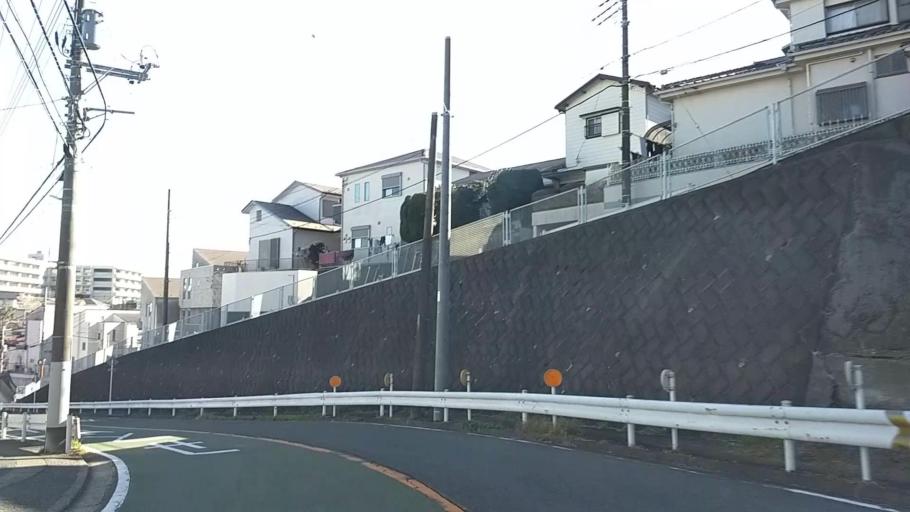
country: JP
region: Kanagawa
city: Yokohama
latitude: 35.4505
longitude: 139.5819
